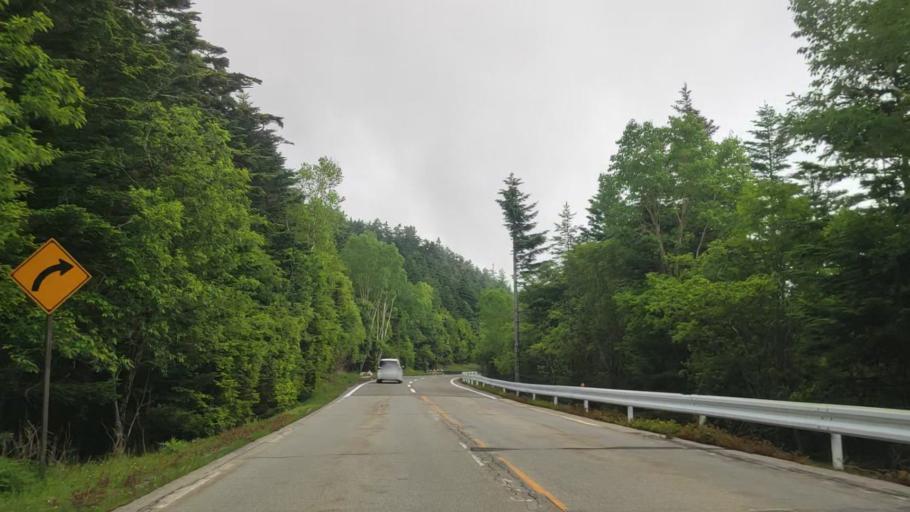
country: JP
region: Yamanashi
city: Fujikawaguchiko
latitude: 35.3840
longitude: 138.6910
